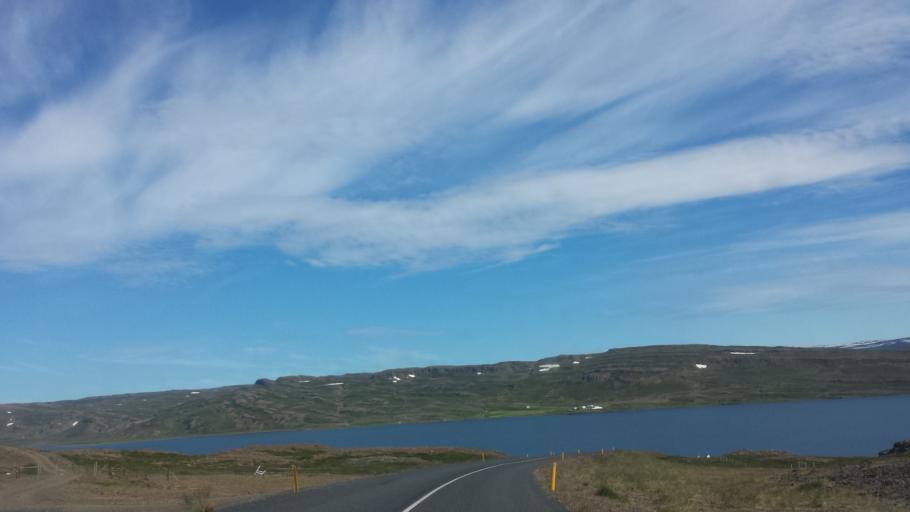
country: IS
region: West
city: Stykkisholmur
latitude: 65.7437
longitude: -21.7086
